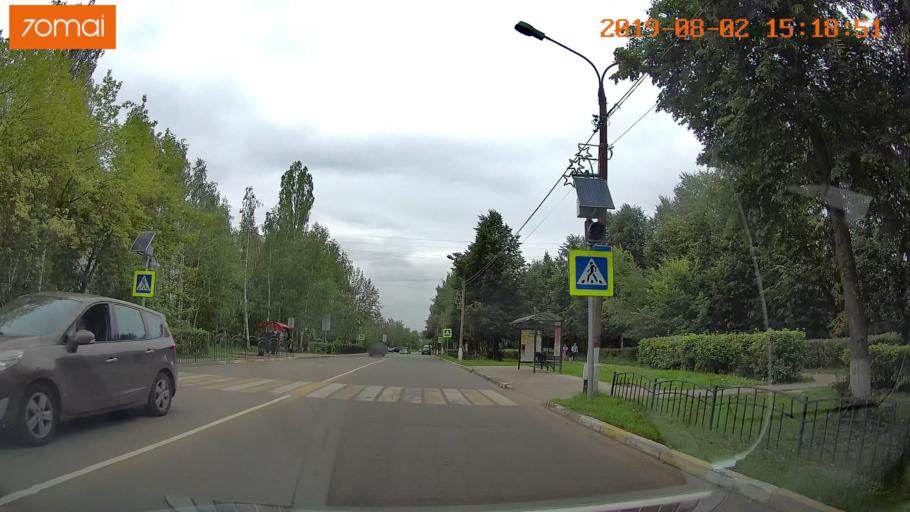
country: RU
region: Moskovskaya
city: Voskresensk
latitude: 55.3117
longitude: 38.6495
